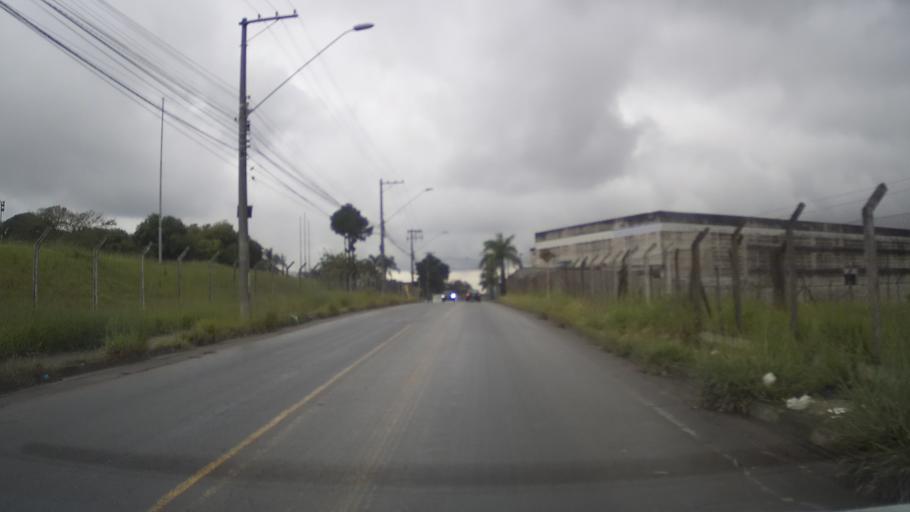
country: BR
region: Sao Paulo
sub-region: Guarulhos
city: Guarulhos
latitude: -23.4715
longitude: -46.4472
